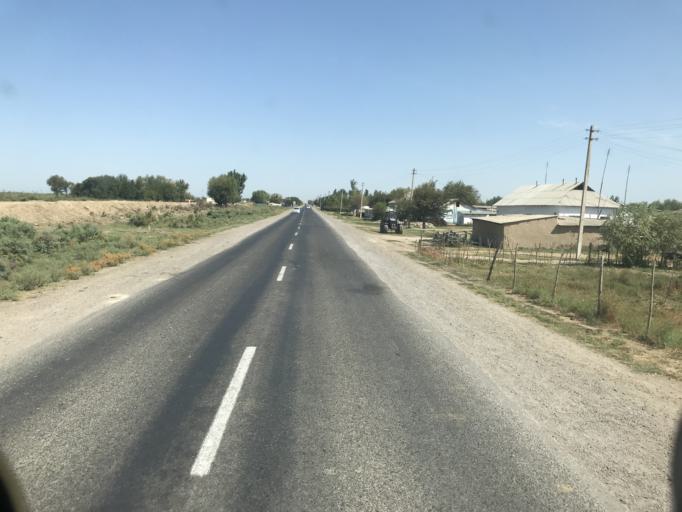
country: KZ
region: Ongtustik Qazaqstan
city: Myrzakent
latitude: 40.7567
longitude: 68.5370
